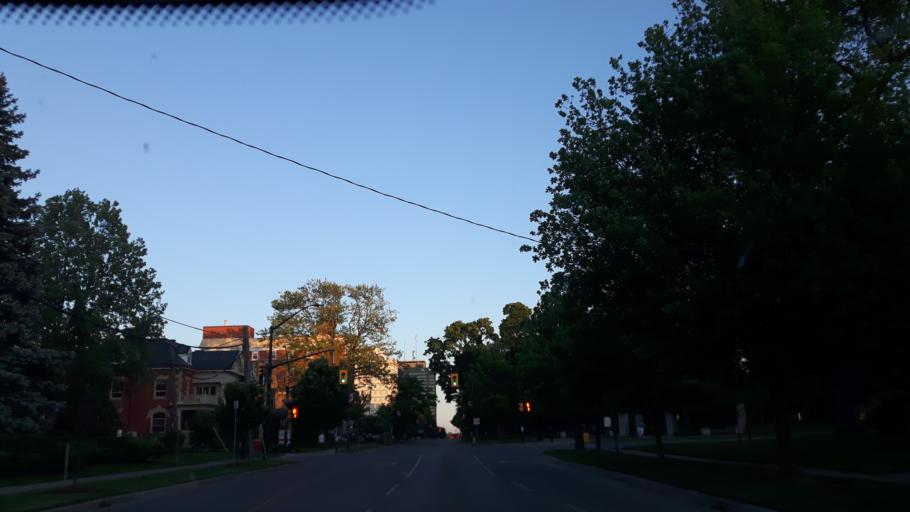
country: CA
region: Ontario
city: London
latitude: 42.9915
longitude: -81.2486
